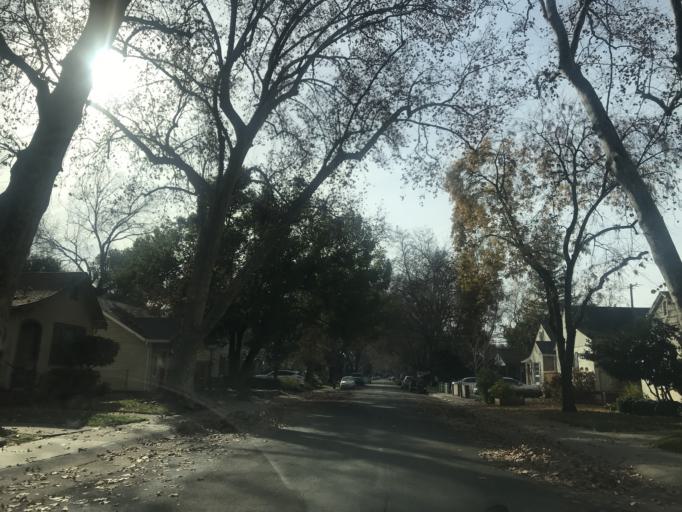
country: US
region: California
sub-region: Sacramento County
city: Sacramento
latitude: 38.5604
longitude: -121.4926
